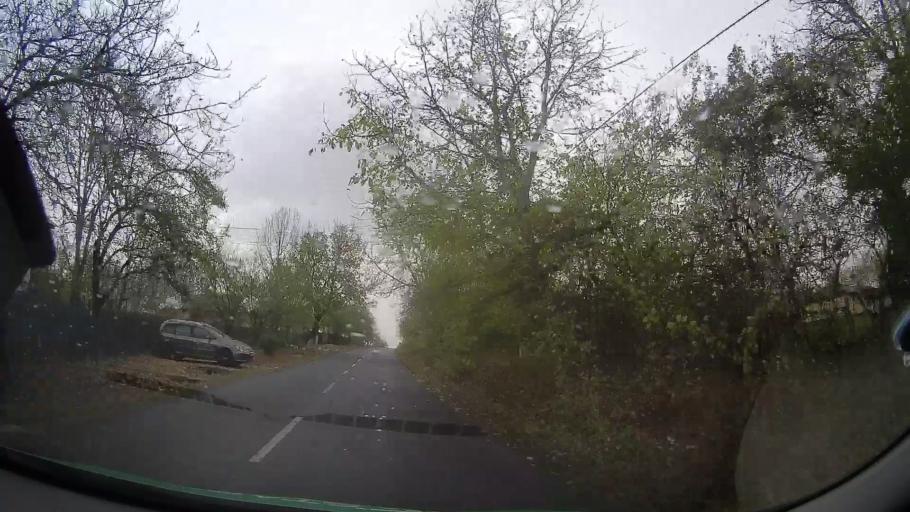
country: RO
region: Ialomita
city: Brazii
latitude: 44.7835
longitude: 26.3200
